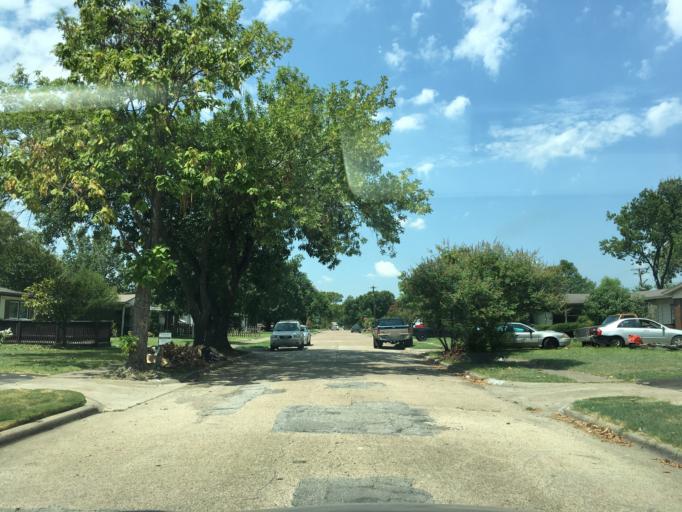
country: US
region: Texas
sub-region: Dallas County
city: Garland
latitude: 32.8625
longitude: -96.6775
